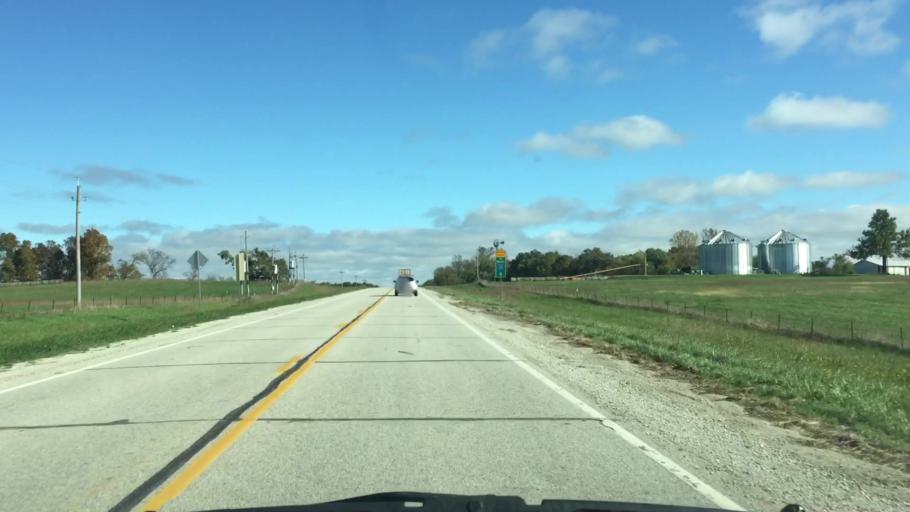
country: US
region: Iowa
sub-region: Decatur County
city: Leon
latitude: 40.6467
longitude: -93.8039
